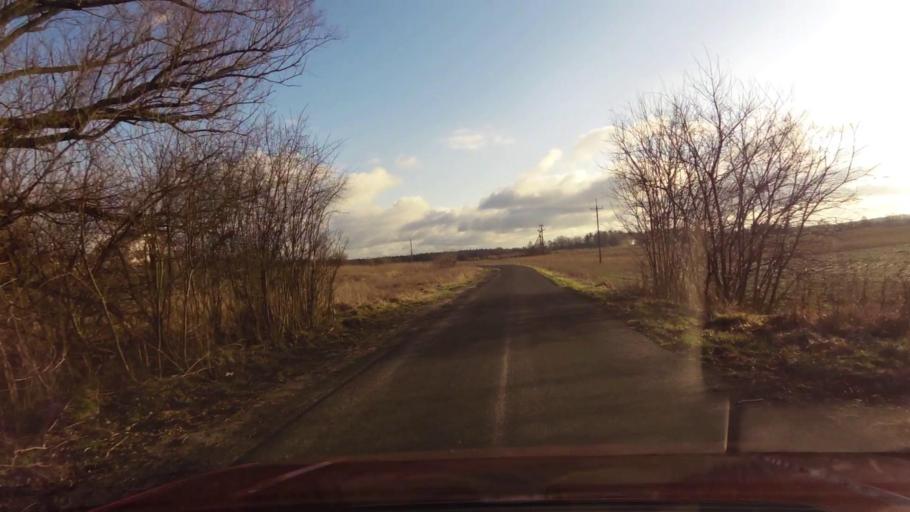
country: PL
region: West Pomeranian Voivodeship
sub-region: Koszalin
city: Koszalin
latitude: 54.0659
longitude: 16.1577
